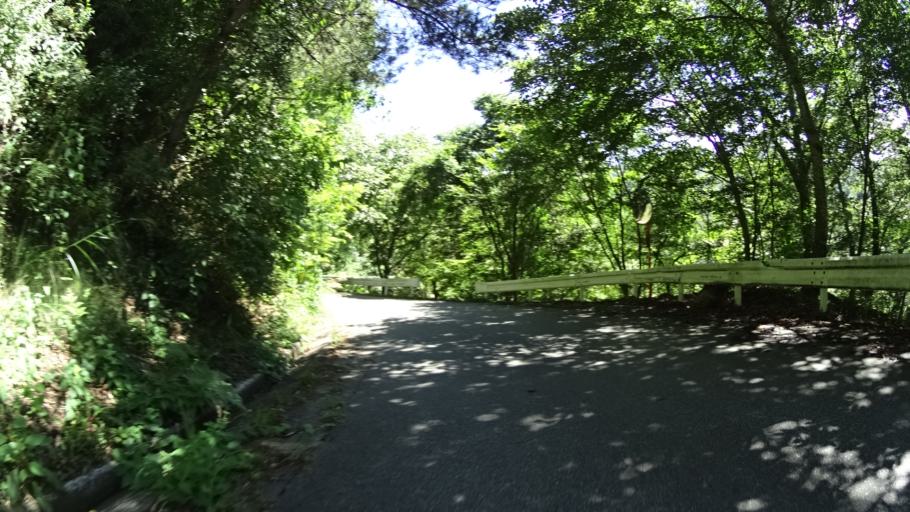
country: JP
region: Yamanashi
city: Enzan
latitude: 35.7428
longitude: 138.8232
